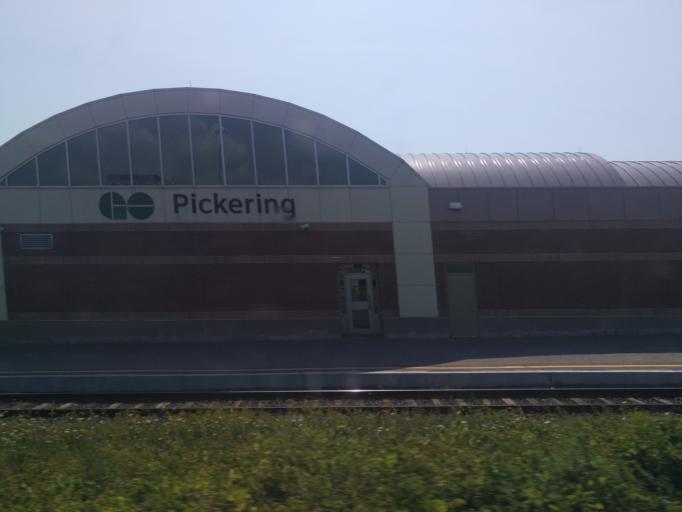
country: CA
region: Ontario
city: Ajax
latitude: 43.8308
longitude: -79.0857
